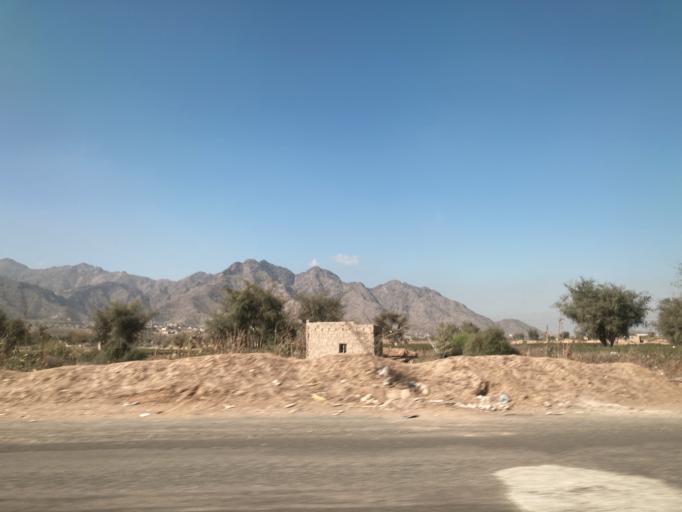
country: YE
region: Ad Dali'
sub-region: Qa'atabah
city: Qa`tabah
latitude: 13.8105
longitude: 44.7220
